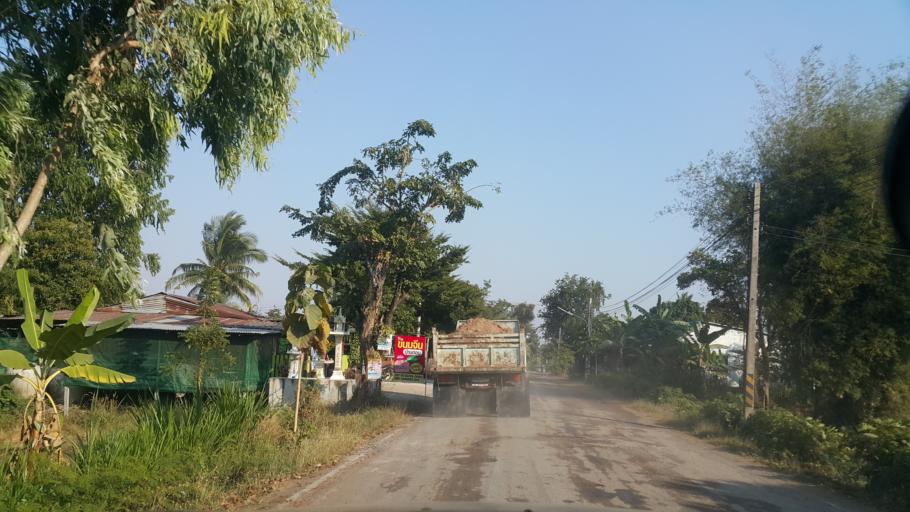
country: TH
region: Nakhon Ratchasima
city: Chakkarat
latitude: 15.0691
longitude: 102.3958
